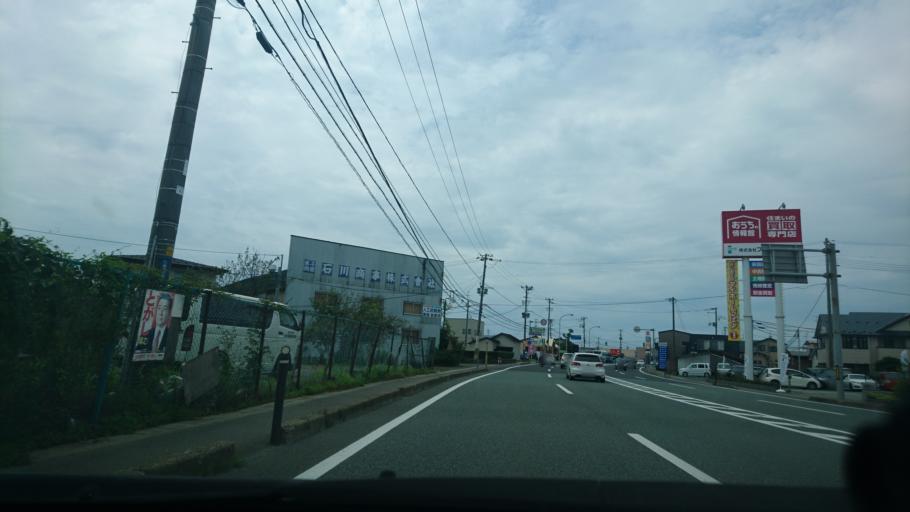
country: JP
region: Akita
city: Akita
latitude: 39.6757
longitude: 140.1308
